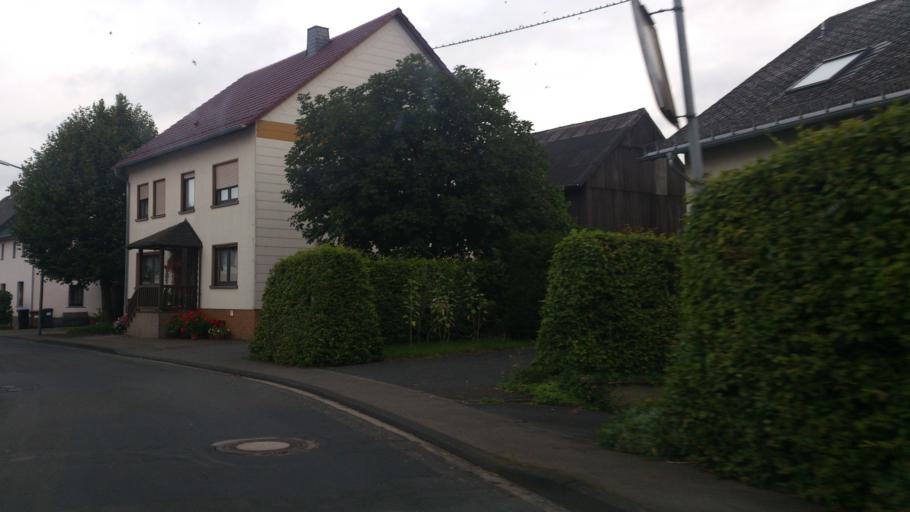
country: DE
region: Rheinland-Pfalz
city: Nohn
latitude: 50.3283
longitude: 6.7867
